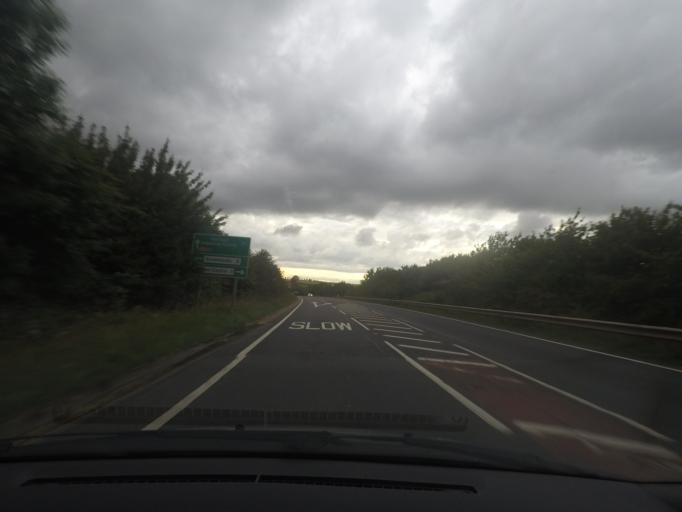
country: GB
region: England
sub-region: Lincolnshire
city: Louth
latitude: 53.3523
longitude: -0.0191
